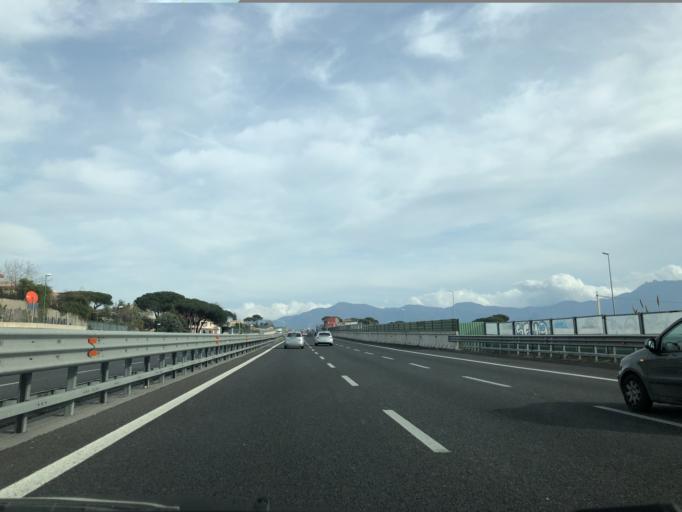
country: IT
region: Campania
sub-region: Provincia di Napoli
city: Torre del Greco
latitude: 40.7748
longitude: 14.4070
